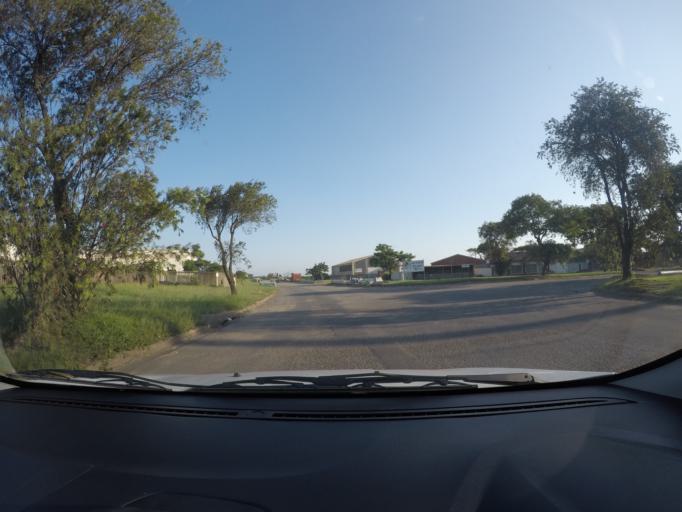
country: ZA
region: KwaZulu-Natal
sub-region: uThungulu District Municipality
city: Richards Bay
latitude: -28.7694
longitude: 32.0097
